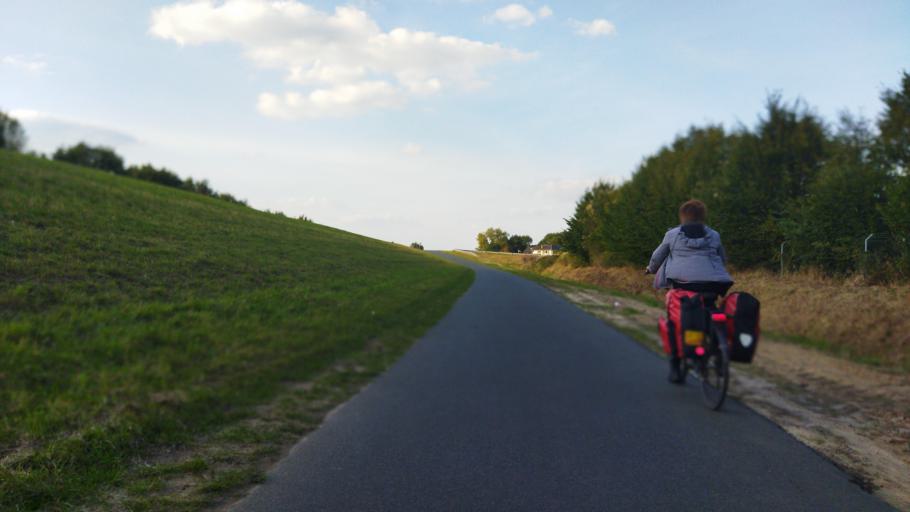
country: DE
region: Lower Saxony
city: Lehe
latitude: 53.0454
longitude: 7.3195
